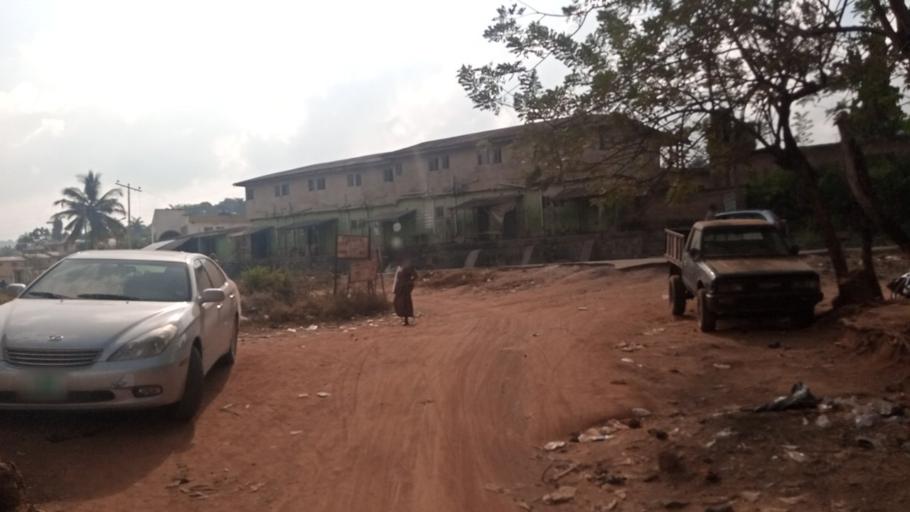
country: NG
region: Osun
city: Iragbiji
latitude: 7.9336
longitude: 4.7137
